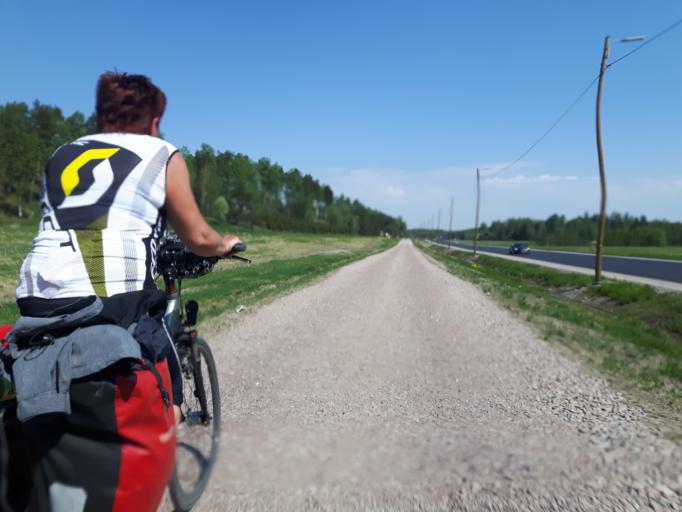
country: FI
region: Uusimaa
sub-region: Helsinki
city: Pornainen
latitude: 60.3450
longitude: 25.4861
